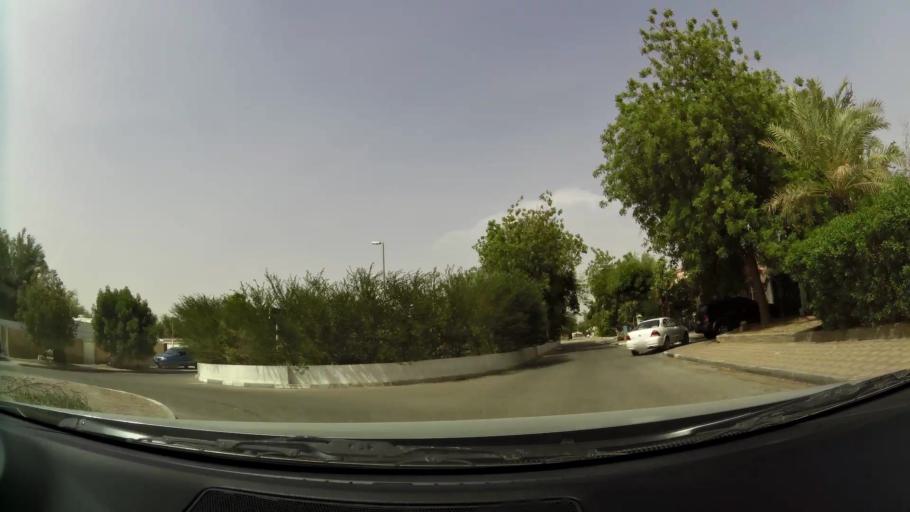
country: AE
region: Abu Dhabi
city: Al Ain
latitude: 24.1872
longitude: 55.6308
